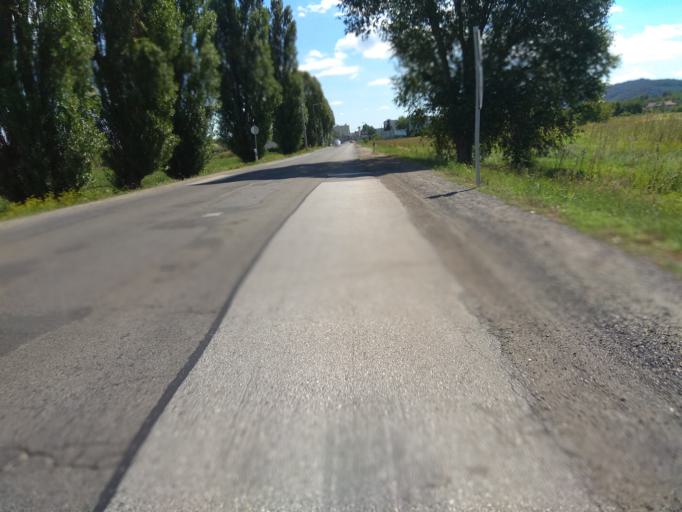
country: HU
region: Borsod-Abauj-Zemplen
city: Kazincbarcika
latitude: 48.2627
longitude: 20.6137
